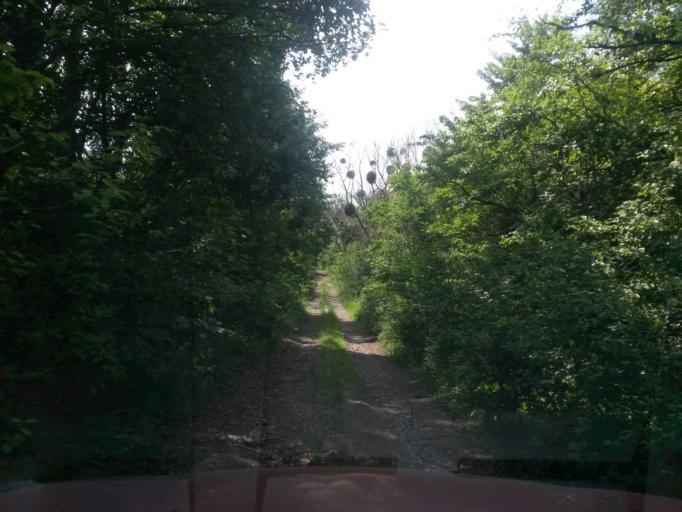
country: SK
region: Kosicky
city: Secovce
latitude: 48.6282
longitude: 21.4917
